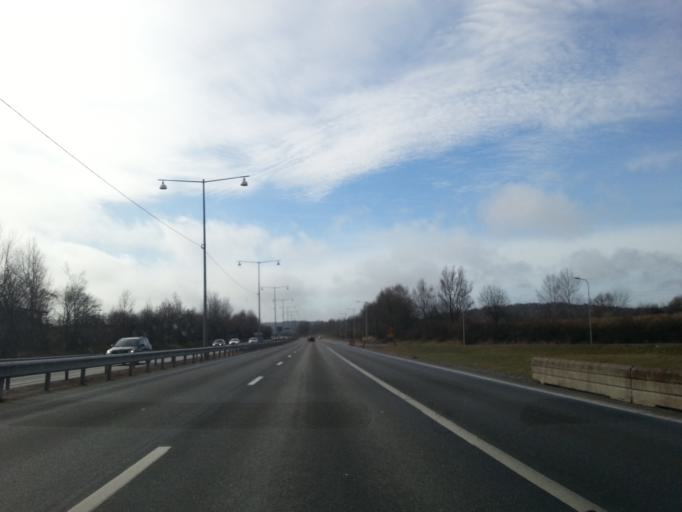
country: SE
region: Vaestra Goetaland
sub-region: Goteborg
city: Gardsten
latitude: 57.7959
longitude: 12.0052
